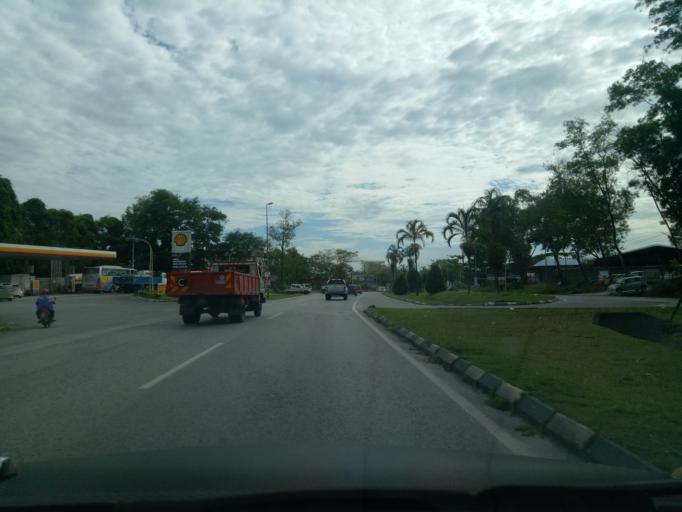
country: MY
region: Sarawak
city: Kuching
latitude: 1.4580
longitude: 110.3251
